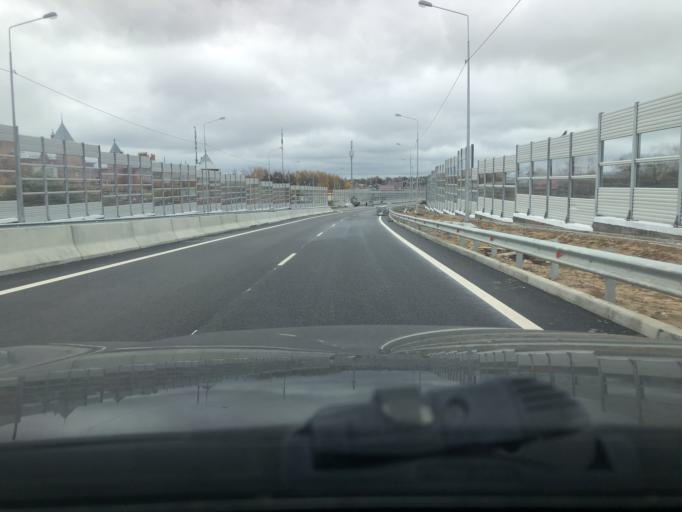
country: RU
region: Moskovskaya
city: Sergiyev Posad
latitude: 56.3091
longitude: 38.0988
